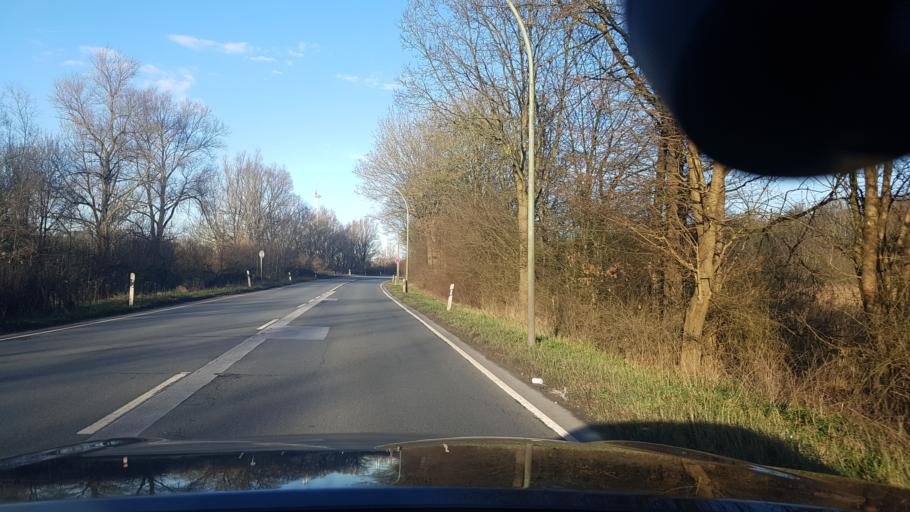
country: DE
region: Bremen
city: Bremerhaven
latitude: 53.5822
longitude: 8.5718
